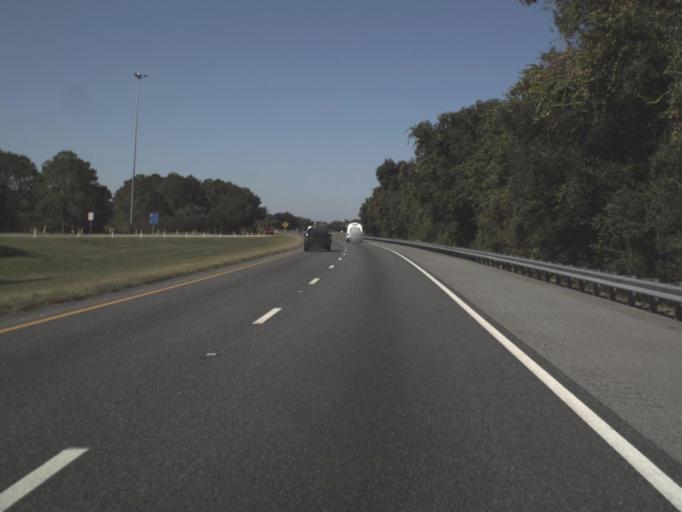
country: US
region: Florida
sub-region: Sumter County
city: Wildwood
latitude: 28.7883
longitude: -81.9826
